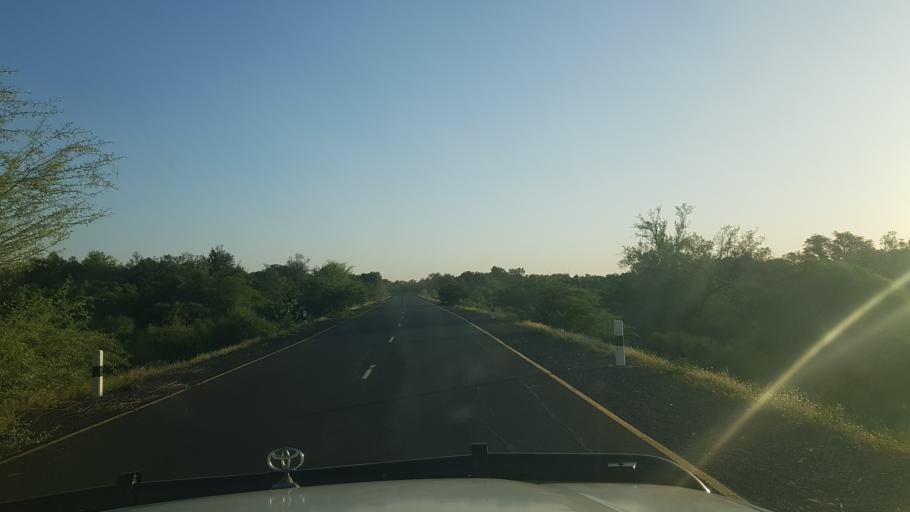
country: ET
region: Southern Nations, Nationalities, and People's Region
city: Lobuni
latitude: 5.1725
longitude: 36.0885
